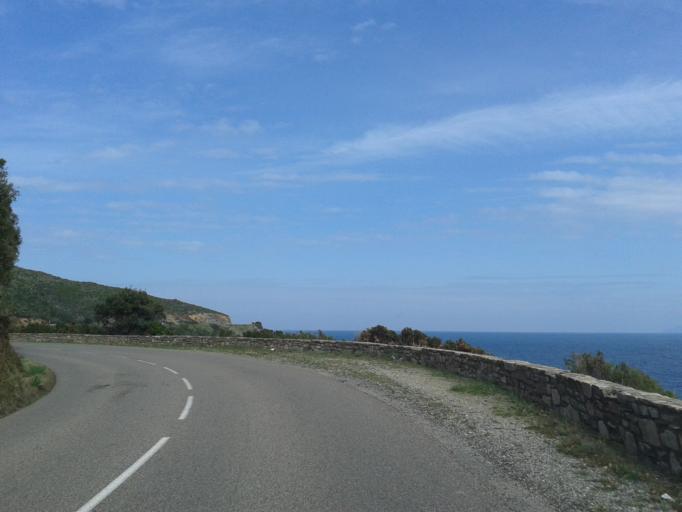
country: FR
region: Corsica
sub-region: Departement de la Haute-Corse
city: Brando
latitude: 42.8454
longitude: 9.4830
